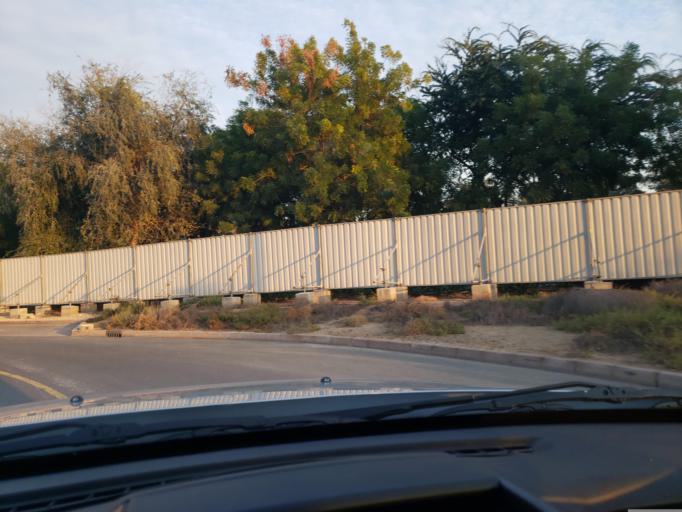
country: AE
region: Dubai
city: Dubai
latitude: 25.0255
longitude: 55.2662
